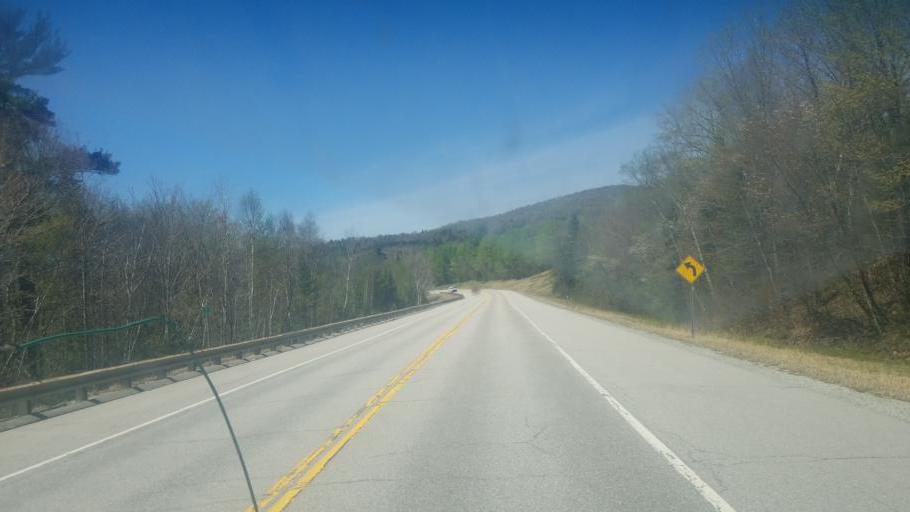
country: US
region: New Hampshire
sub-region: Grafton County
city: Deerfield
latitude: 44.2707
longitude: -71.5126
